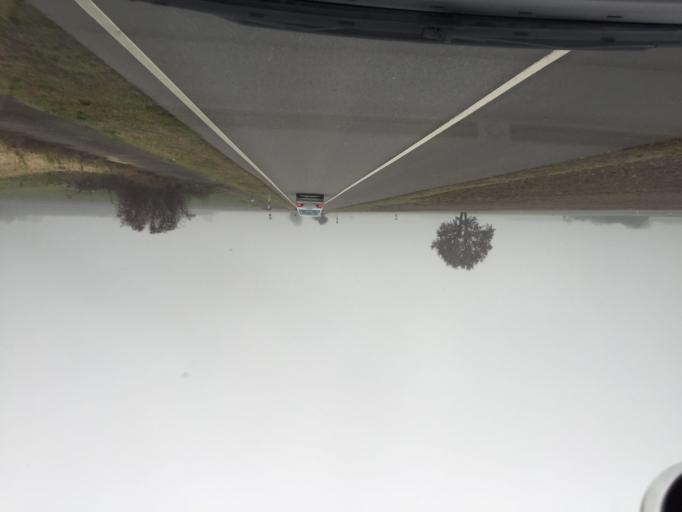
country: DE
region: Baden-Wuerttemberg
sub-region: Freiburg Region
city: Hartheim
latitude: 47.9807
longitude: 7.6453
